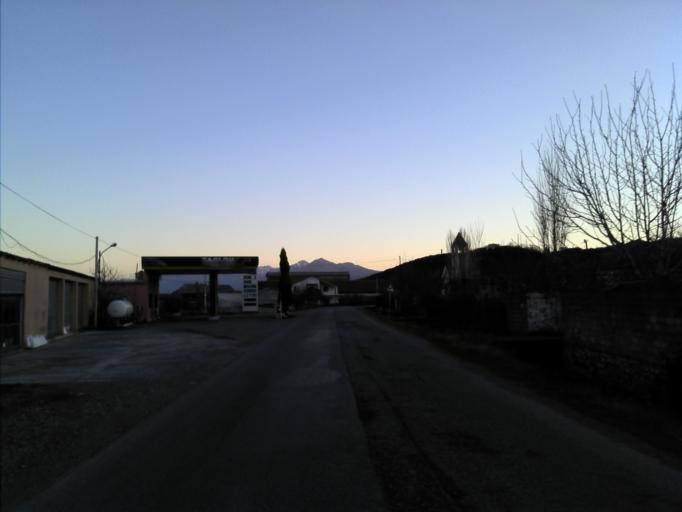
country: AL
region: Shkoder
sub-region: Rrethi i Shkodres
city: Berdica e Madhe
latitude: 42.0145
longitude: 19.4818
